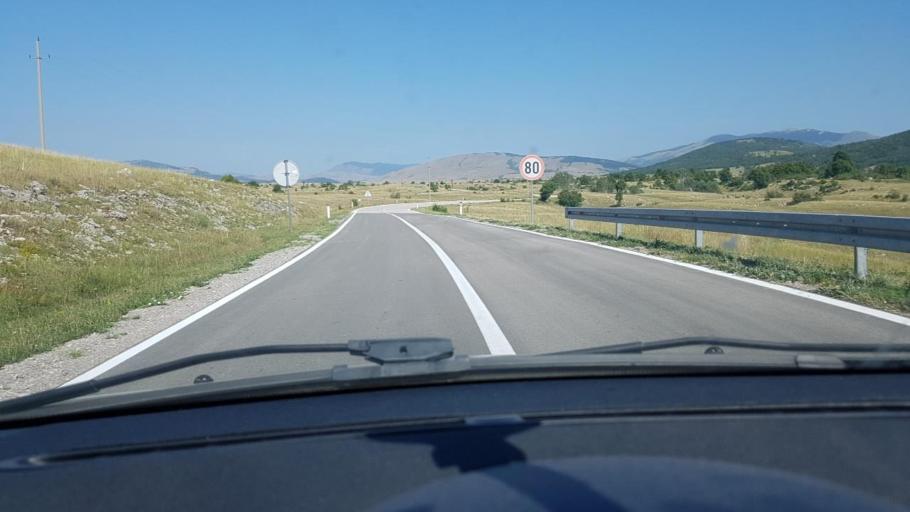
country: BA
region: Federation of Bosnia and Herzegovina
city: Bosansko Grahovo
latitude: 44.1366
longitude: 16.4754
